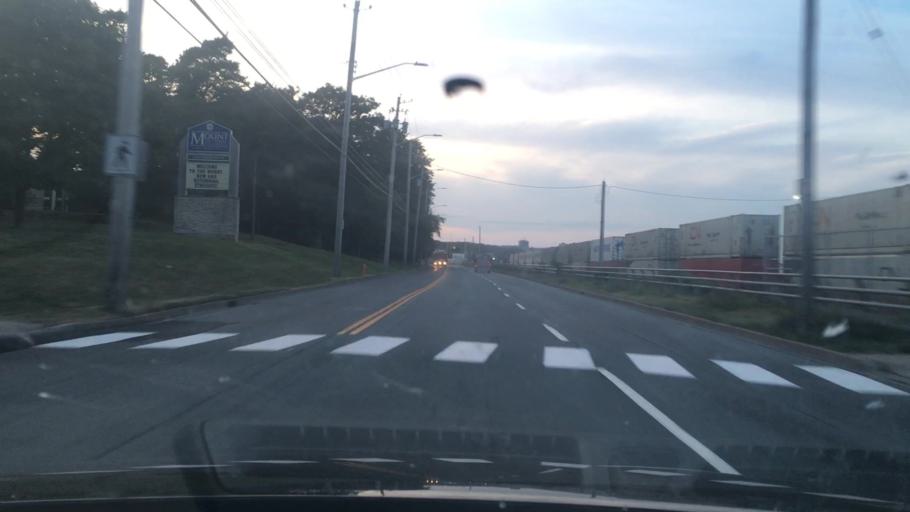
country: CA
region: Nova Scotia
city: Dartmouth
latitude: 44.6705
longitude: -63.6417
